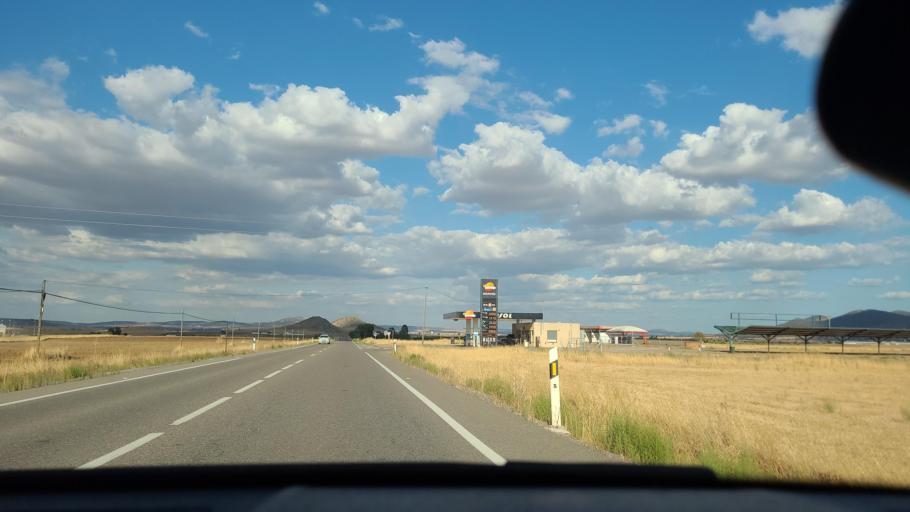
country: ES
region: Andalusia
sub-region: Province of Cordoba
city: Fuente Obejuna
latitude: 38.2750
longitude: -5.4046
